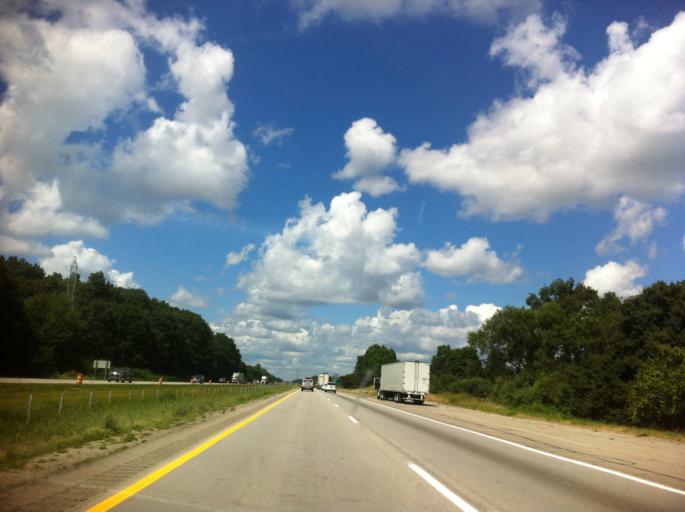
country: US
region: Michigan
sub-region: Washtenaw County
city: Milan
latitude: 42.1775
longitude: -83.6845
